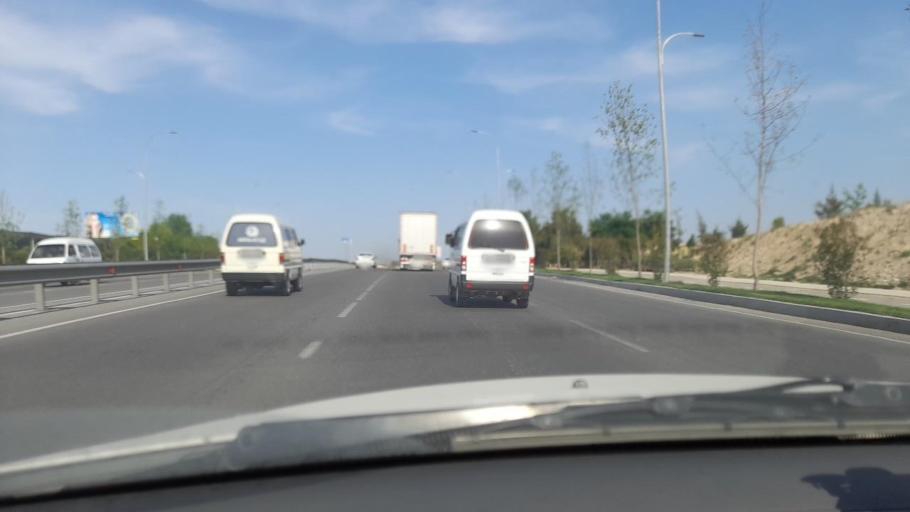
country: UZ
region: Samarqand
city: Jomboy
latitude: 39.6738
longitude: 67.0291
